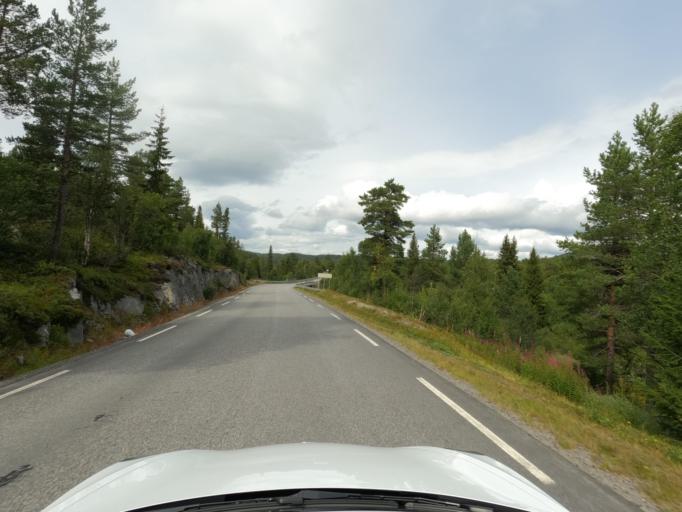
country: NO
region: Telemark
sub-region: Vinje
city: Amot
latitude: 59.7079
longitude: 8.1159
